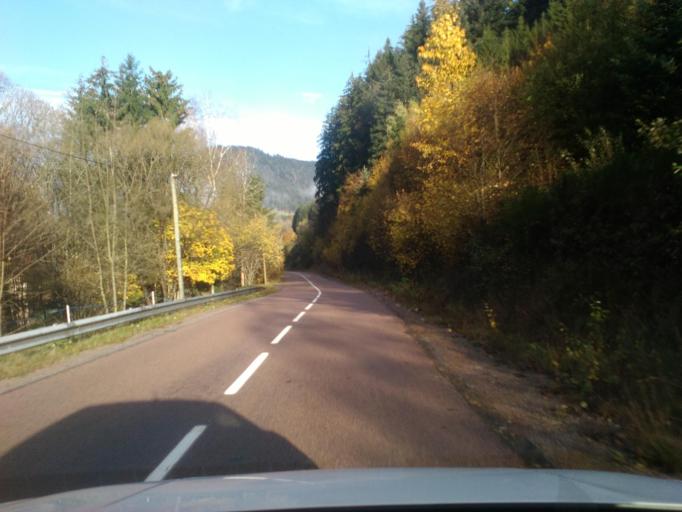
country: FR
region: Lorraine
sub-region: Departement des Vosges
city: Senones
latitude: 48.4253
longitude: 7.0330
